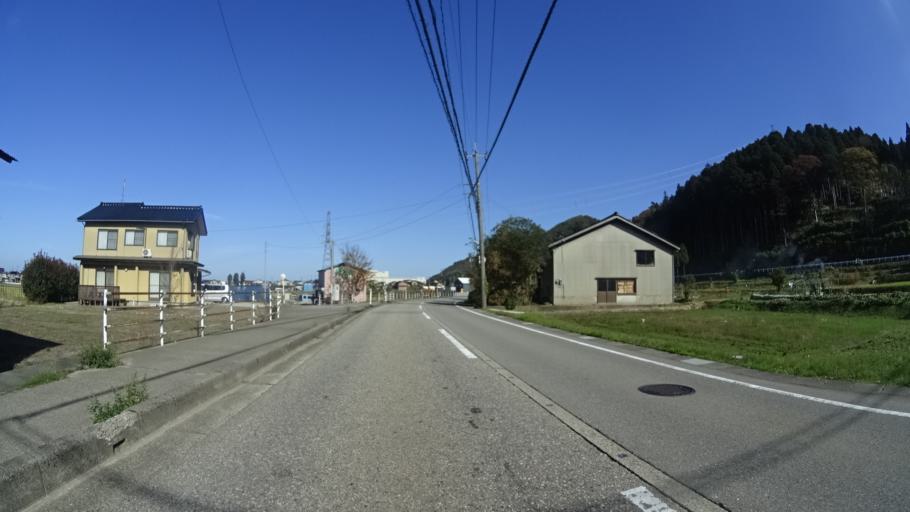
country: JP
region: Ishikawa
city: Tsurugi-asahimachi
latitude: 36.4860
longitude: 136.6166
